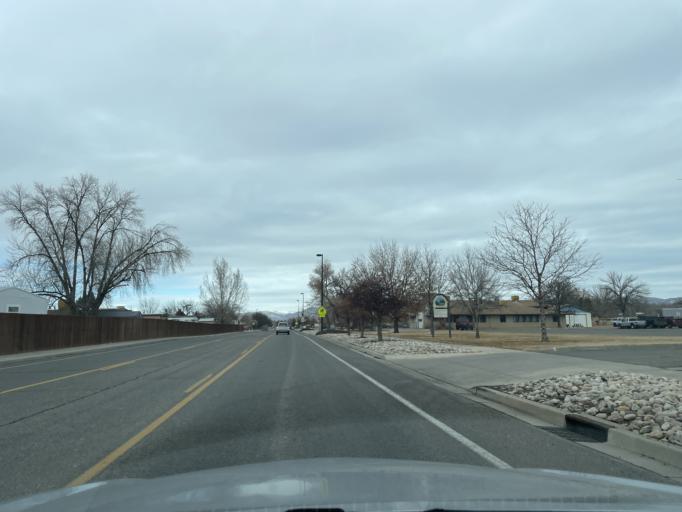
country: US
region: Colorado
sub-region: Mesa County
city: Grand Junction
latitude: 39.0882
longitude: -108.5801
